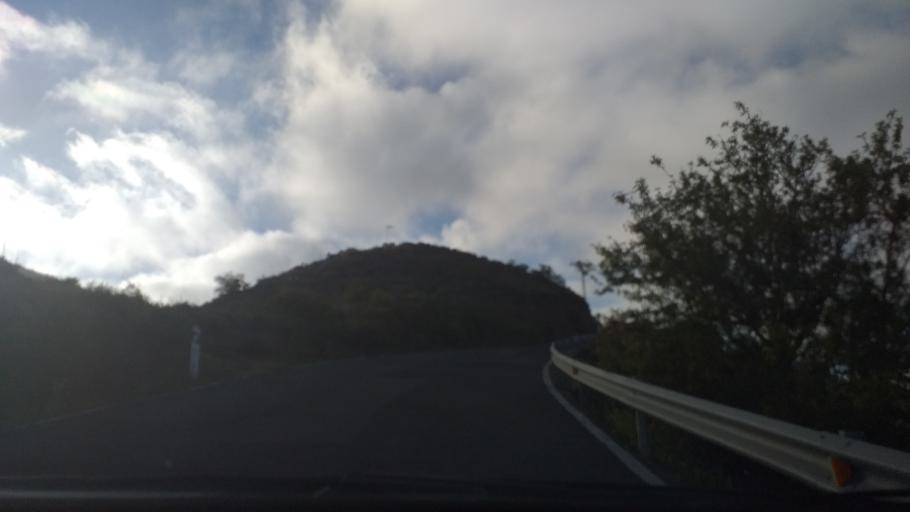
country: ES
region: Canary Islands
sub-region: Provincia de Las Palmas
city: Valsequillo de Gran Canaria
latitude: 27.9575
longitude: -15.4973
